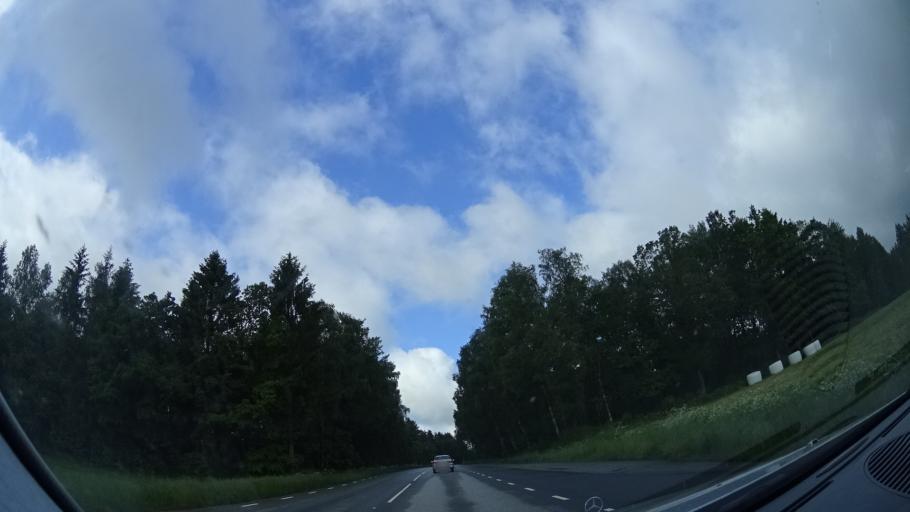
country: SE
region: Skane
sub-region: Eslovs Kommun
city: Stehag
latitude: 55.9442
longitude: 13.4219
